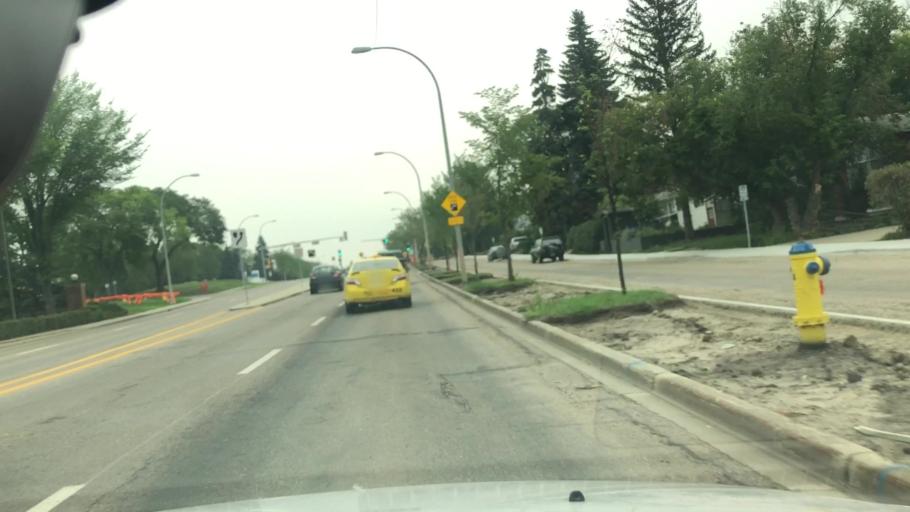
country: CA
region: Alberta
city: Edmonton
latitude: 53.5174
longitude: -113.5315
